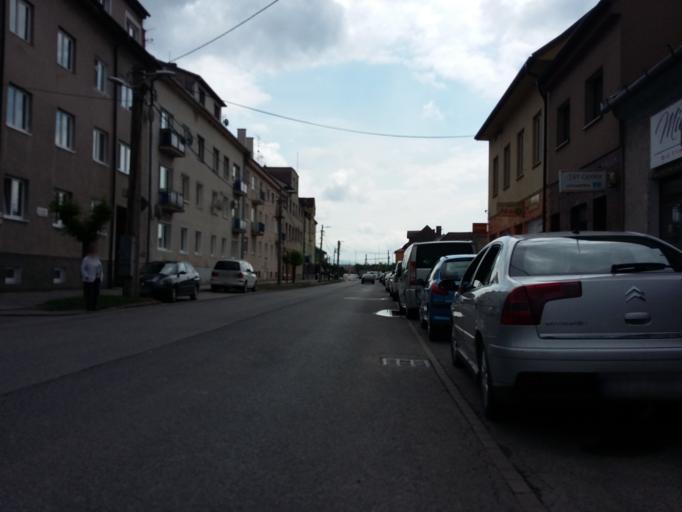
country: SK
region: Bratislavsky
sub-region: Okres Malacky
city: Malacky
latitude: 48.4360
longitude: 17.0204
